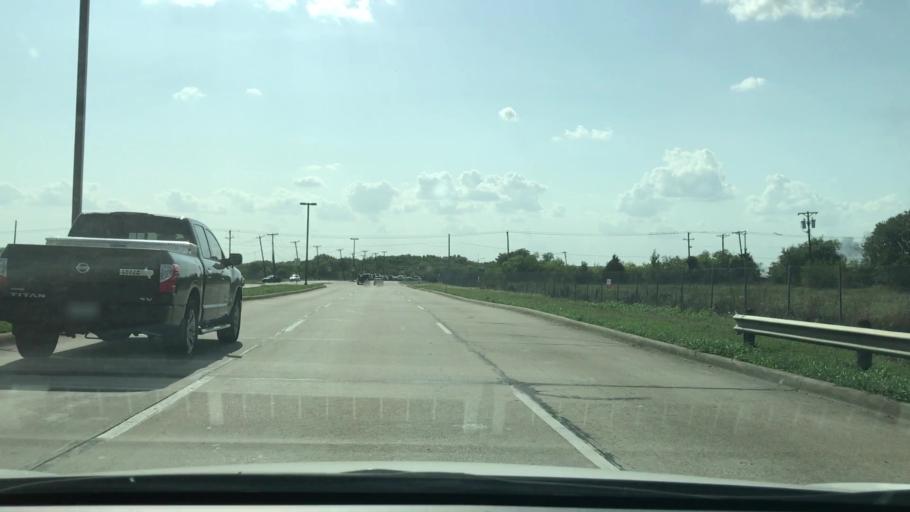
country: US
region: Texas
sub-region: Tarrant County
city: Euless
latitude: 32.8668
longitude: -97.0117
